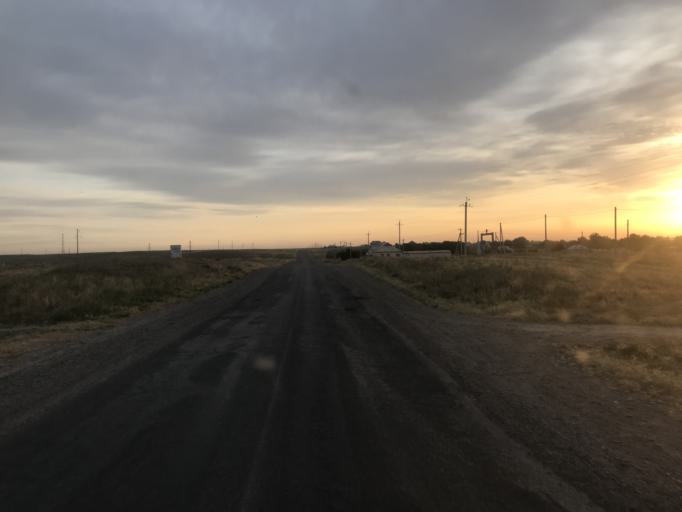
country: UZ
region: Toshkent
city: Amir Timur
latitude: 41.2310
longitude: 68.8085
